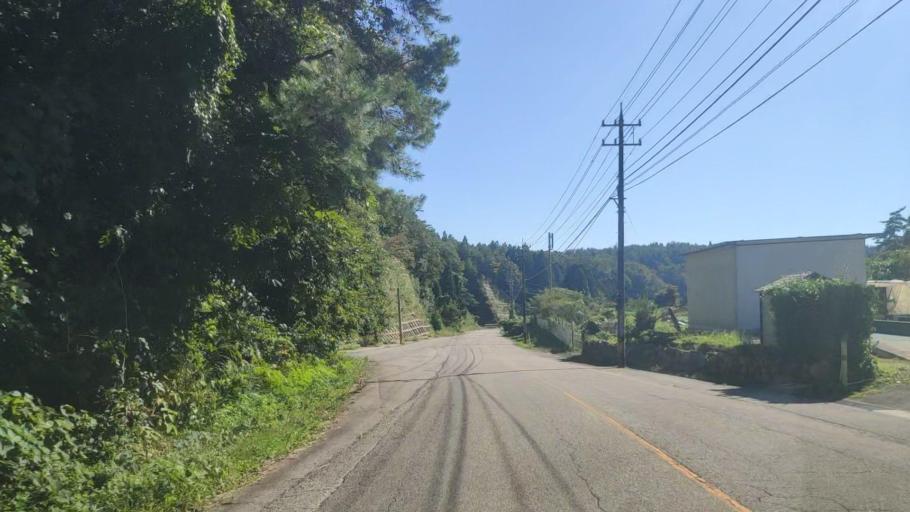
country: JP
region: Ishikawa
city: Nanao
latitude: 37.3182
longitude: 137.1651
